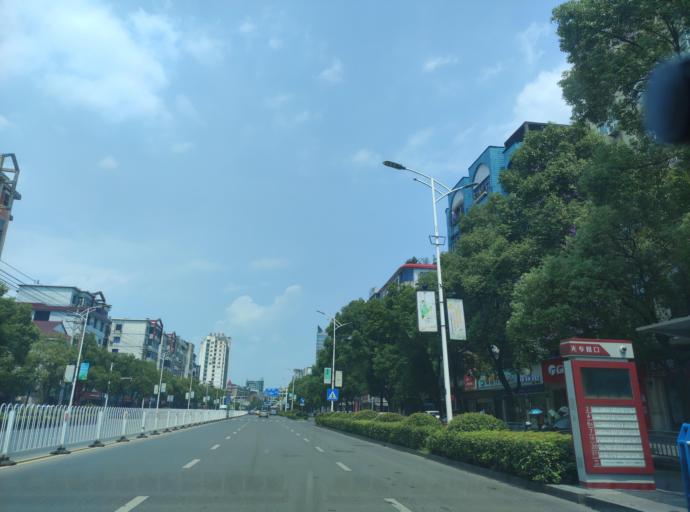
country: CN
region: Jiangxi Sheng
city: Pingxiang
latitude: 27.6392
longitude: 113.8606
